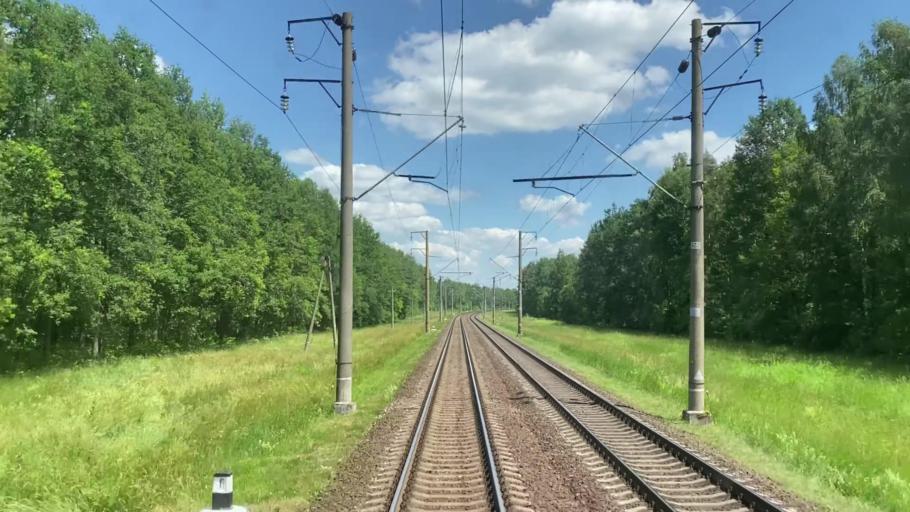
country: BY
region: Brest
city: Pruzhany
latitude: 52.4994
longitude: 24.6162
